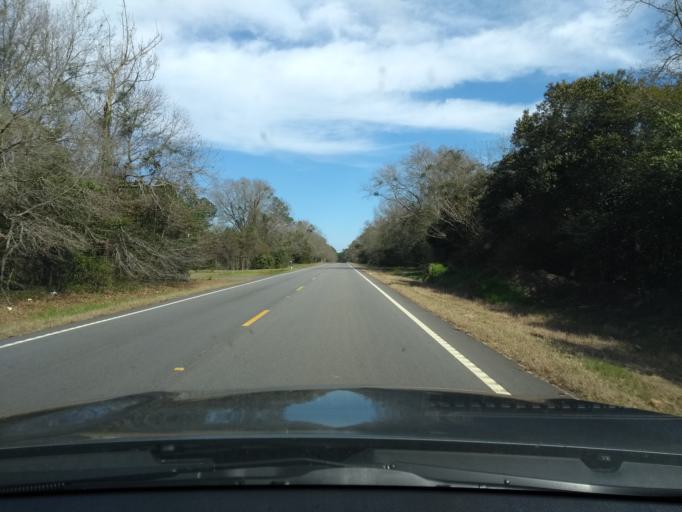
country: US
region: Georgia
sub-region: Bulloch County
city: Brooklet
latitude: 32.4821
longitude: -81.5857
